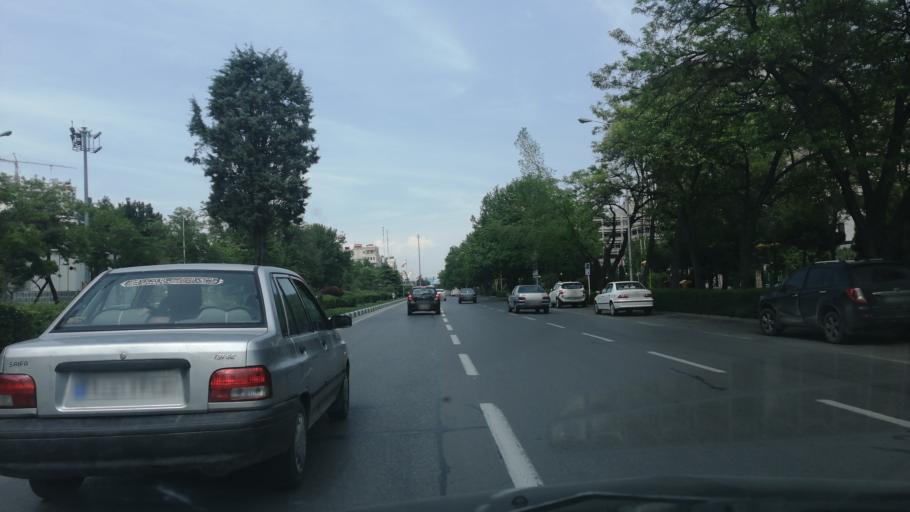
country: IR
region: Razavi Khorasan
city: Mashhad
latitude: 36.3175
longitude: 59.5632
